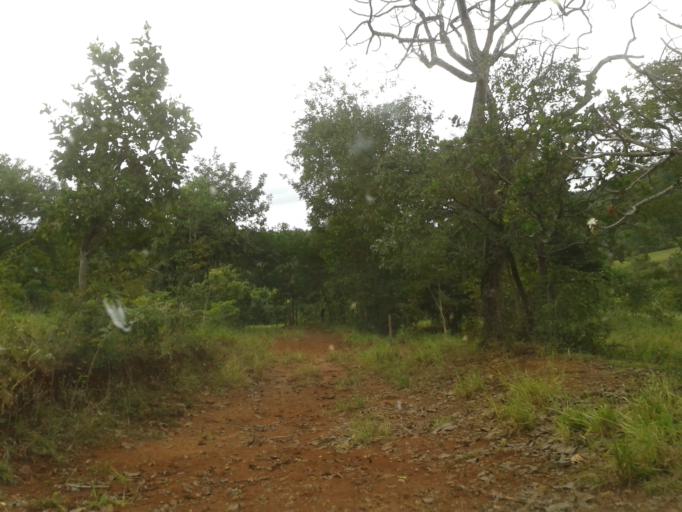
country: BR
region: Minas Gerais
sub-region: Campina Verde
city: Campina Verde
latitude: -19.4591
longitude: -49.5843
